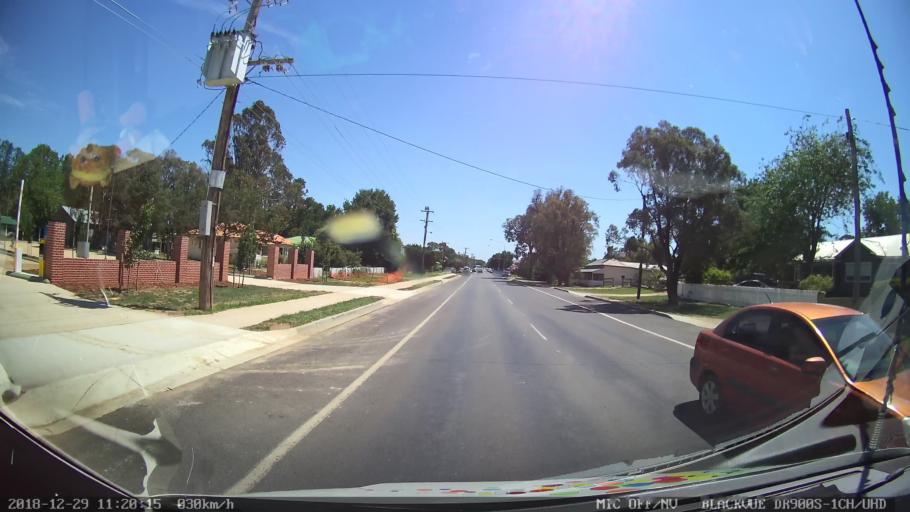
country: AU
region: New South Wales
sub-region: Palerang
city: Bungendore
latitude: -35.2578
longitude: 149.4401
